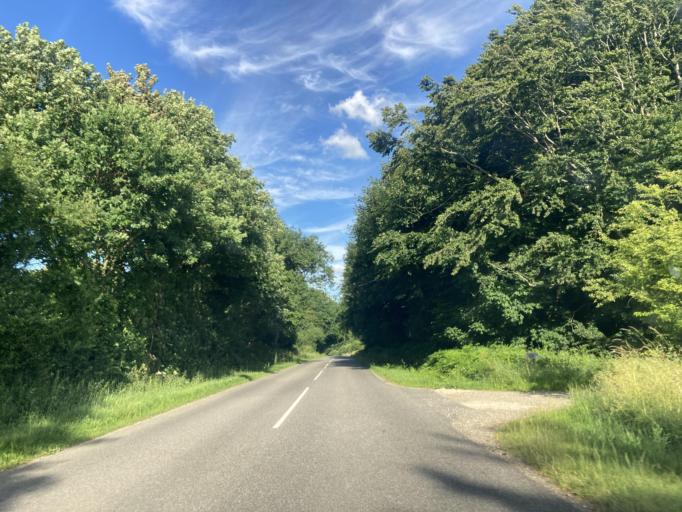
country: DK
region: South Denmark
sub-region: Kolding Kommune
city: Lunderskov
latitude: 55.4839
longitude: 9.3722
